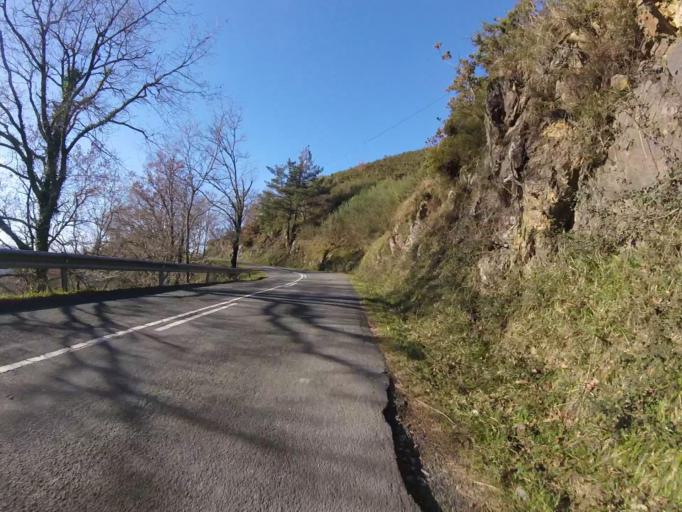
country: ES
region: Basque Country
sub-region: Provincia de Guipuzcoa
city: Irun
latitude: 43.2932
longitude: -1.8129
